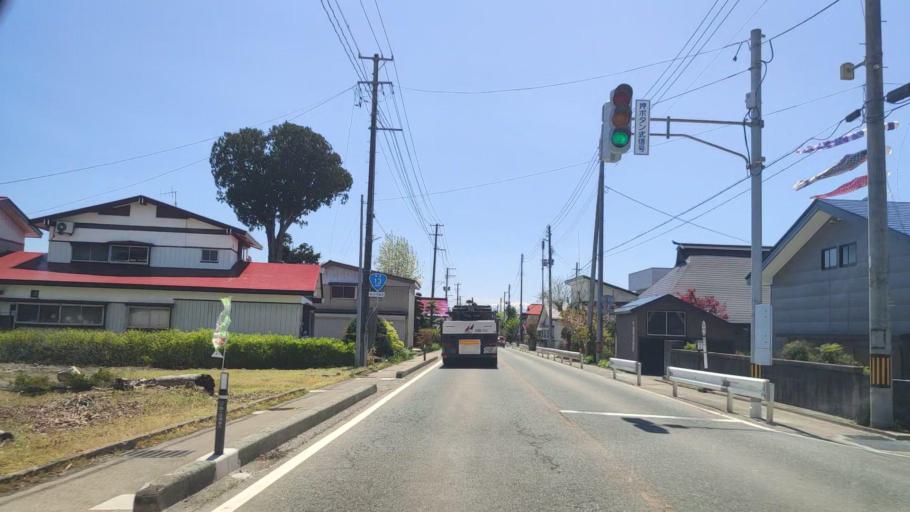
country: JP
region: Yamagata
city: Shinjo
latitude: 38.8043
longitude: 140.3210
